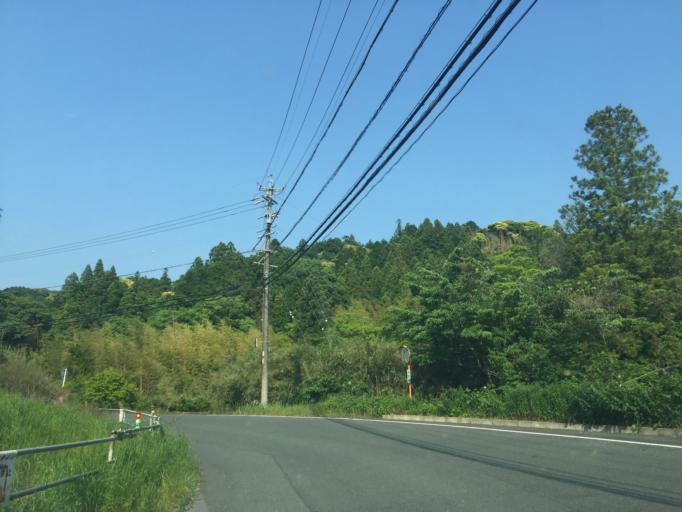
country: JP
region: Shizuoka
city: Kakegawa
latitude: 34.8247
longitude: 138.0426
